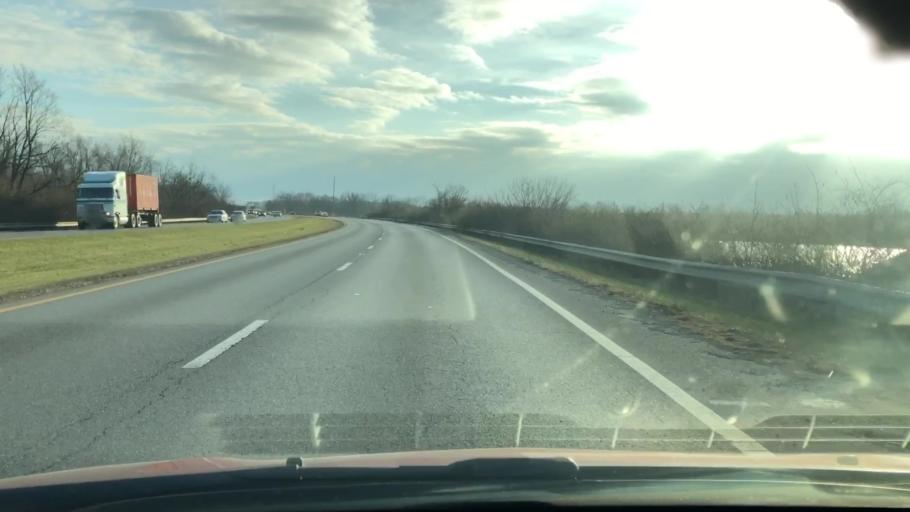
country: US
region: Ohio
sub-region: Franklin County
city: Obetz
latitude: 39.8623
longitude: -82.9378
